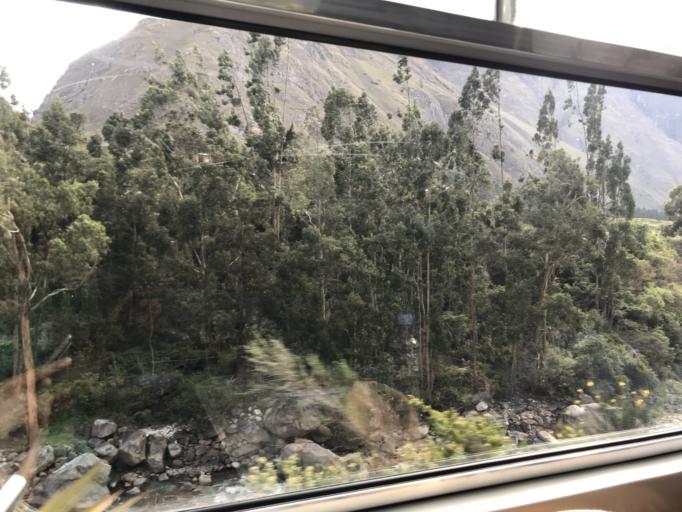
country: PE
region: Cusco
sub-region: Provincia de Urubamba
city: Ollantaytambo
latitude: -13.2256
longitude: -72.4229
